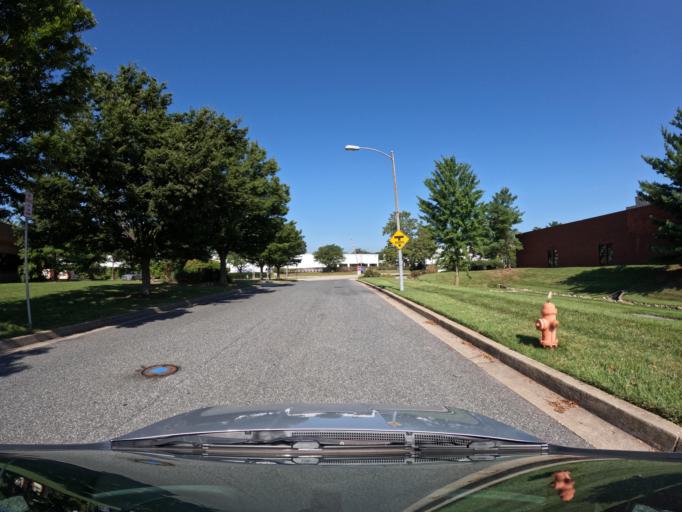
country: US
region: Maryland
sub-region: Baltimore County
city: Cockeysville
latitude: 39.4785
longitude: -76.6619
